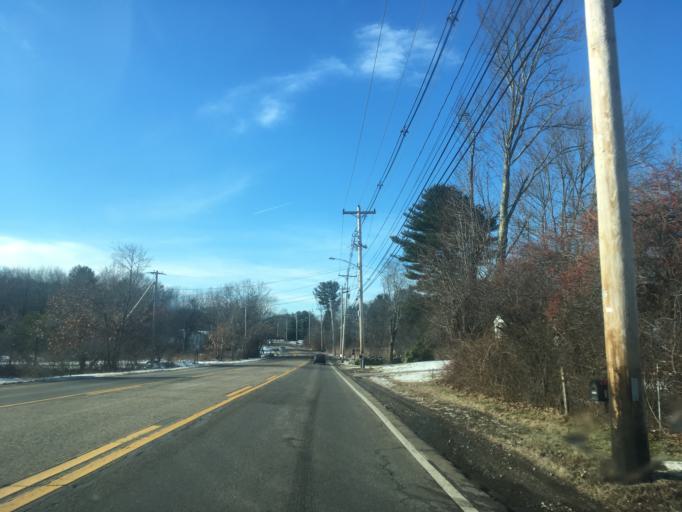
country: US
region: Massachusetts
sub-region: Essex County
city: Salisbury
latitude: 42.8444
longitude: -70.8809
